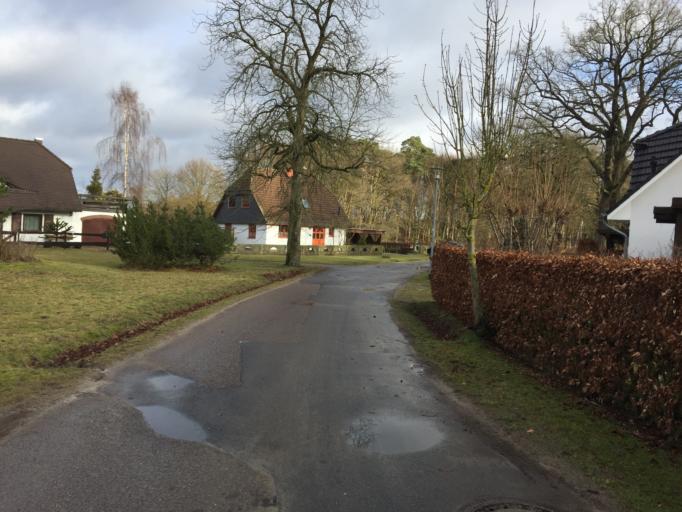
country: DE
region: Mecklenburg-Vorpommern
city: Rovershagen
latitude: 54.1821
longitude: 12.2282
